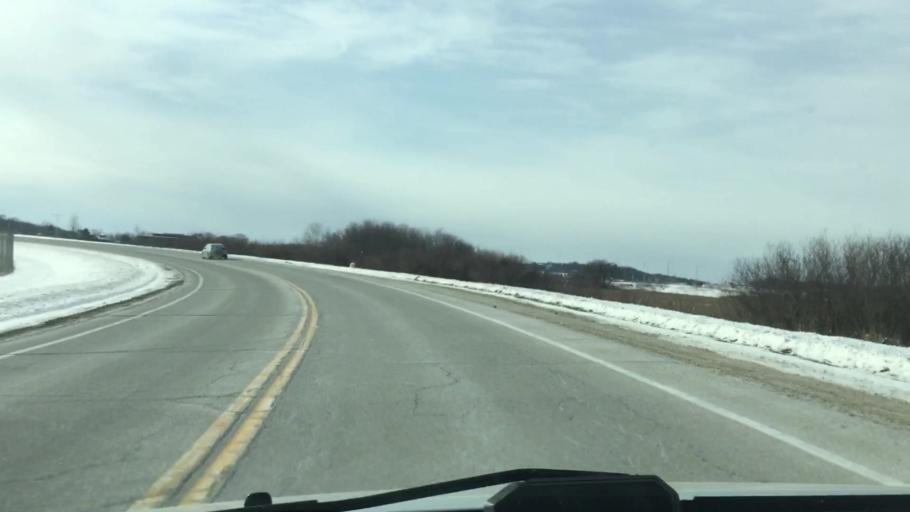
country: US
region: Wisconsin
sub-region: Waukesha County
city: Pewaukee
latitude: 43.0454
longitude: -88.2505
